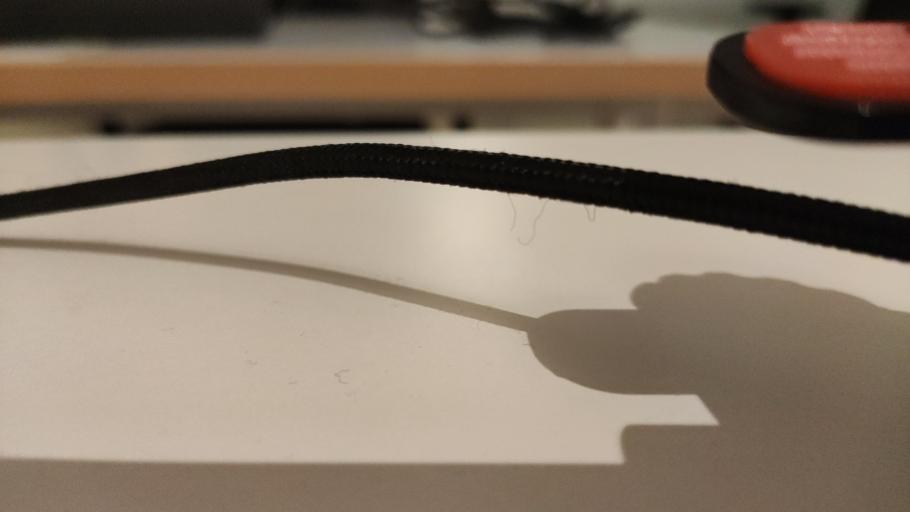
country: RU
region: Moskovskaya
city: Il'inskiy Pogost
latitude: 55.5186
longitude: 38.8717
